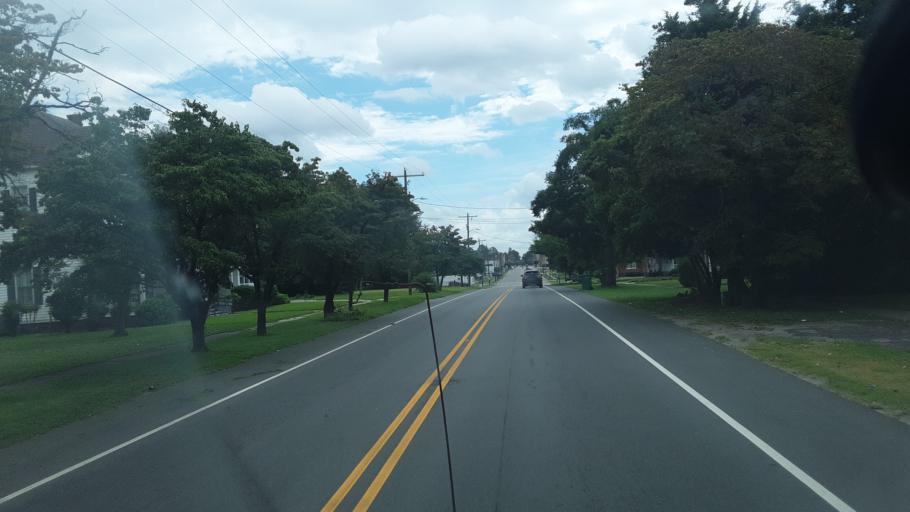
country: US
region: North Carolina
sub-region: Robeson County
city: Rowland
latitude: 34.5395
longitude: -79.2979
